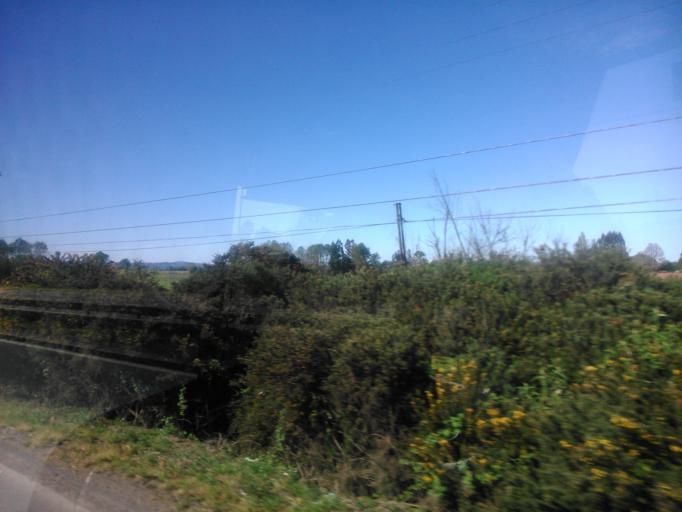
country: CL
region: Araucania
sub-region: Provincia de Cautin
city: Freire
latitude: -38.8862
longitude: -72.6192
